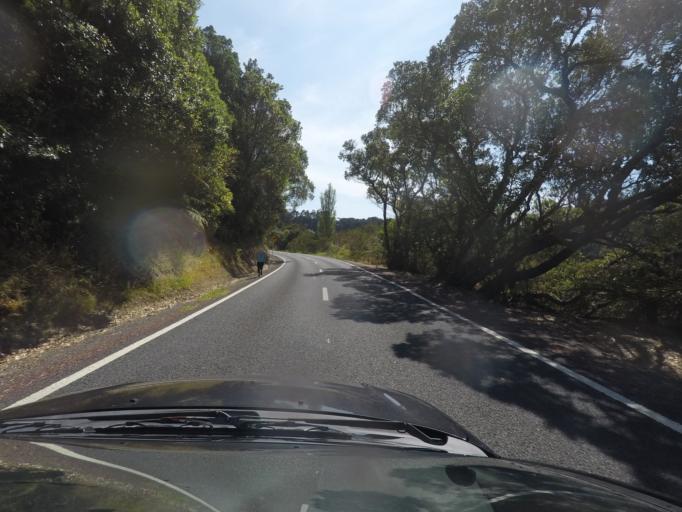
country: NZ
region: Auckland
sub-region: Auckland
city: Warkworth
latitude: -36.3067
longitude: 174.7819
